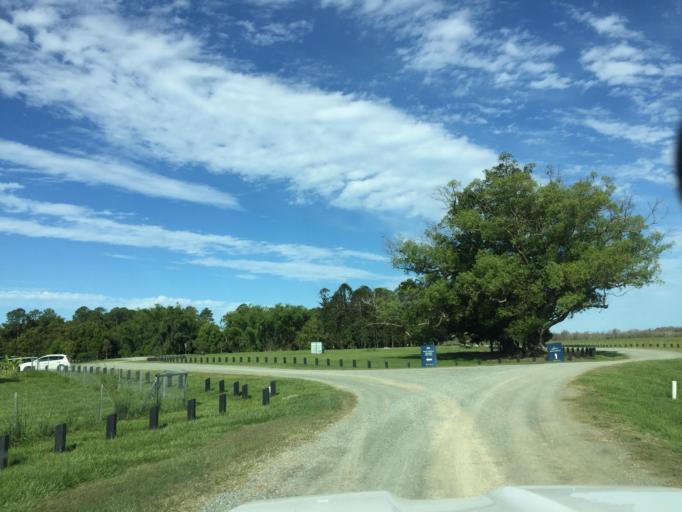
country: AU
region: Queensland
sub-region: Moreton Bay
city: Morayfield
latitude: -27.1067
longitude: 152.9933
